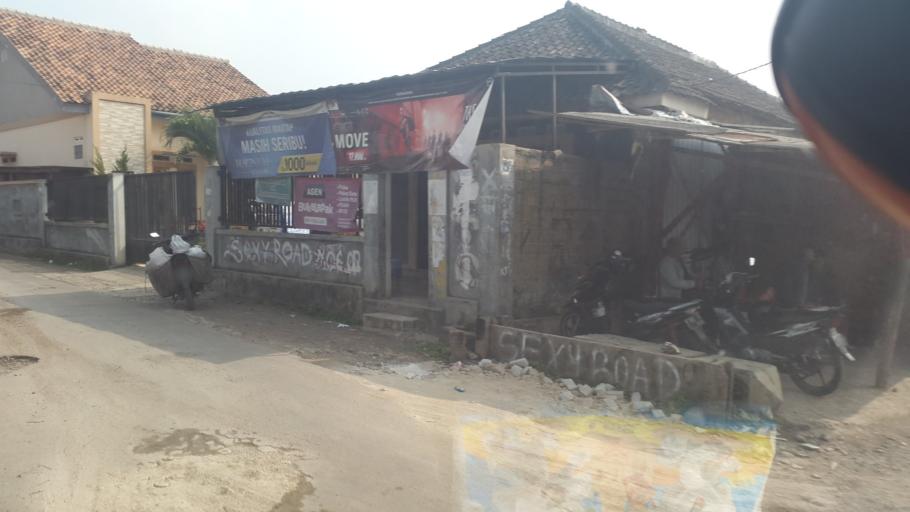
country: ID
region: West Java
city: Sukabumi
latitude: -6.9247
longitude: 106.8937
